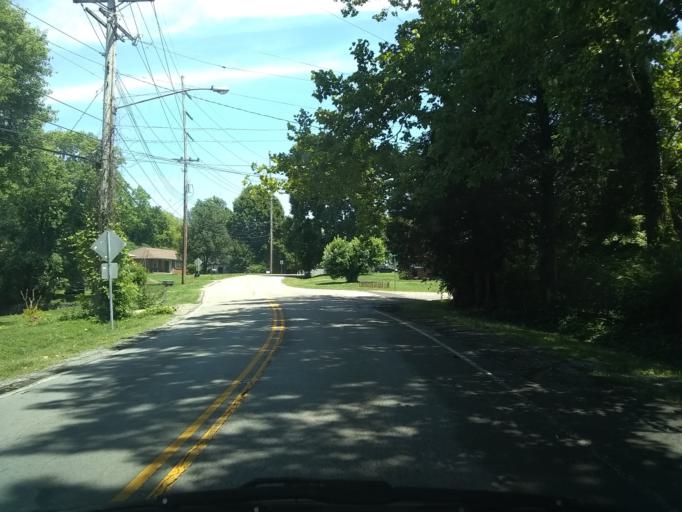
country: US
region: Tennessee
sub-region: Davidson County
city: Nashville
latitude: 36.1355
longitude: -86.7065
